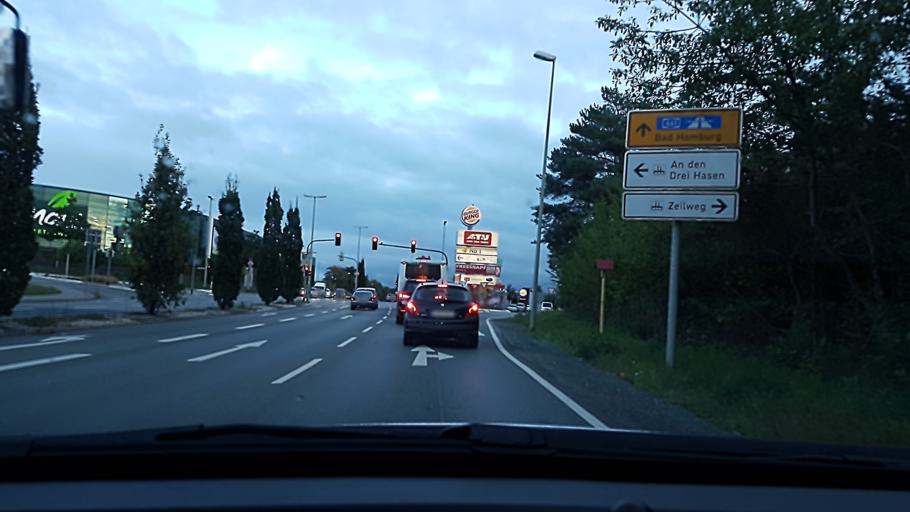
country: DE
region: Hesse
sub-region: Regierungsbezirk Darmstadt
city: Oberursel
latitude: 50.2054
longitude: 8.5998
